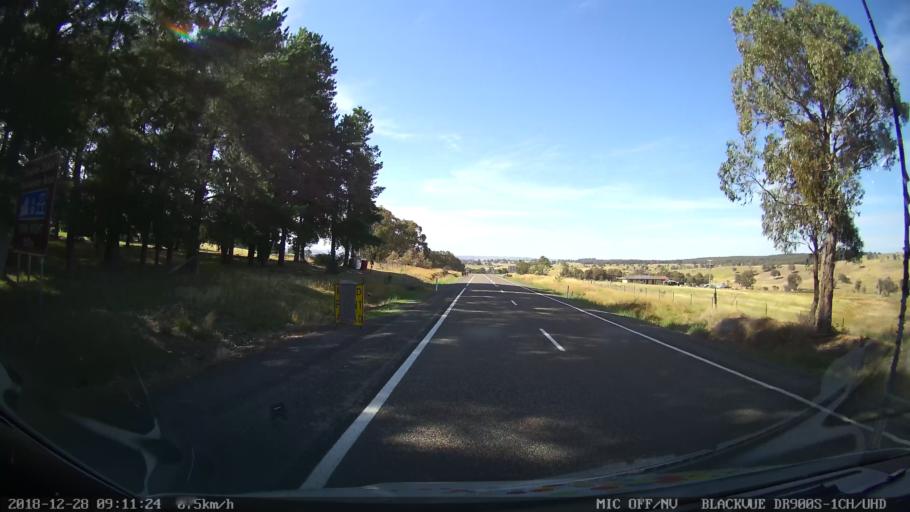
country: AU
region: New South Wales
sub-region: Upper Lachlan Shire
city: Crookwell
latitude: -34.2430
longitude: 149.3384
